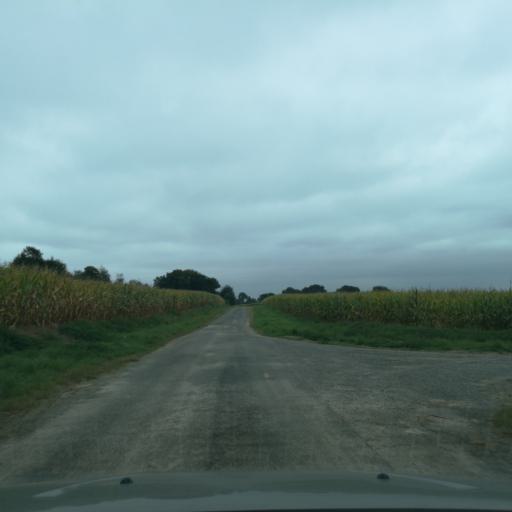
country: FR
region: Brittany
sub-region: Departement d'Ille-et-Vilaine
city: Montauban-de-Bretagne
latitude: 48.1878
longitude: -2.0265
